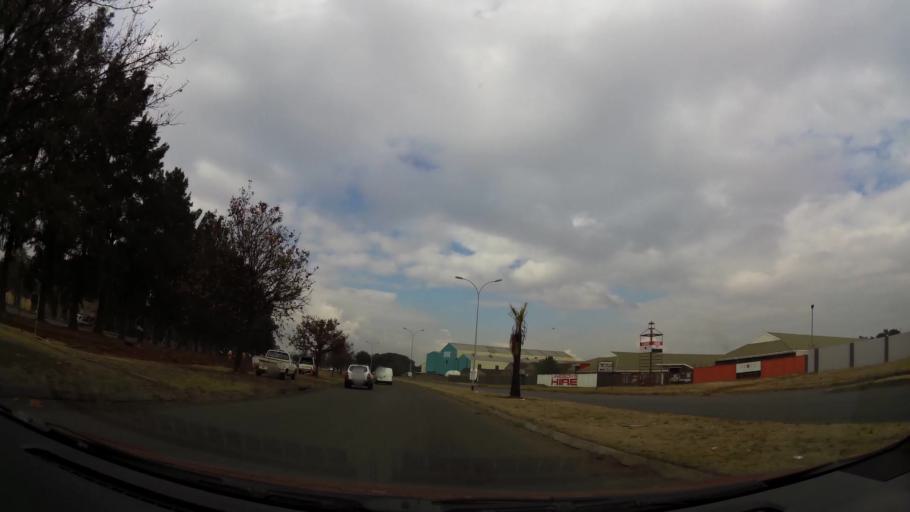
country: ZA
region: Gauteng
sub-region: Sedibeng District Municipality
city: Vanderbijlpark
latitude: -26.7040
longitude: 27.8593
